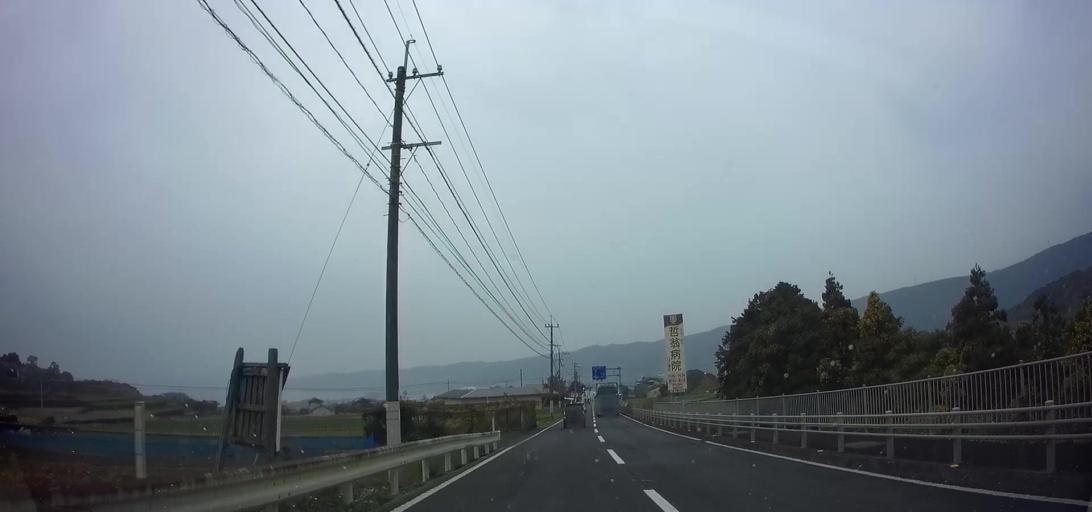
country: JP
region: Nagasaki
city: Shimabara
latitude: 32.7808
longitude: 130.2073
